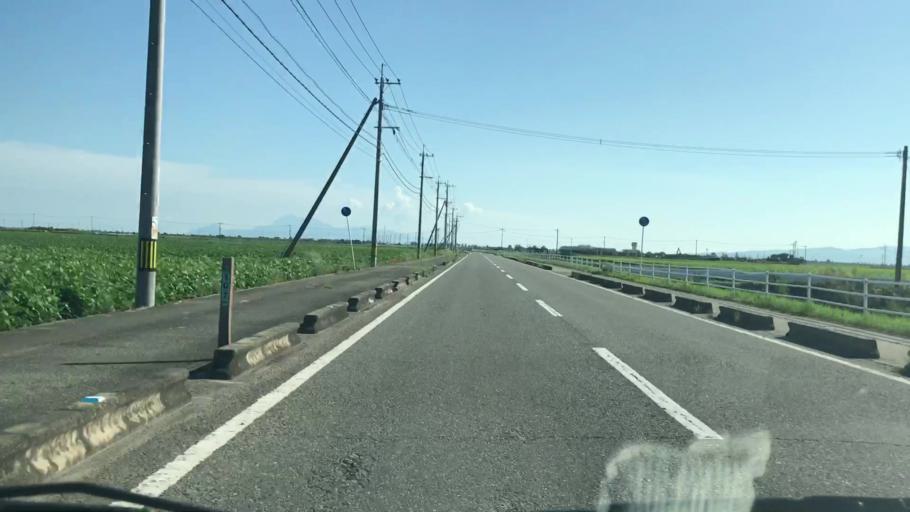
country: JP
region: Saga Prefecture
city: Okawa
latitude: 33.1687
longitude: 130.3099
